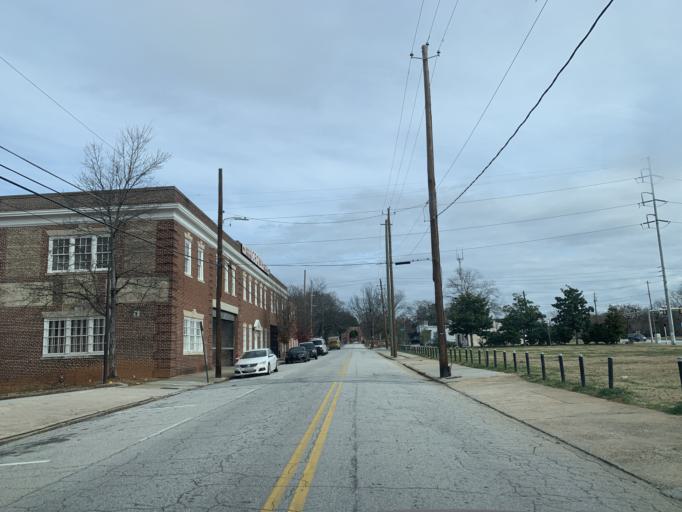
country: US
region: Georgia
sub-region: Fulton County
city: Atlanta
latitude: 33.7474
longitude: -84.3776
